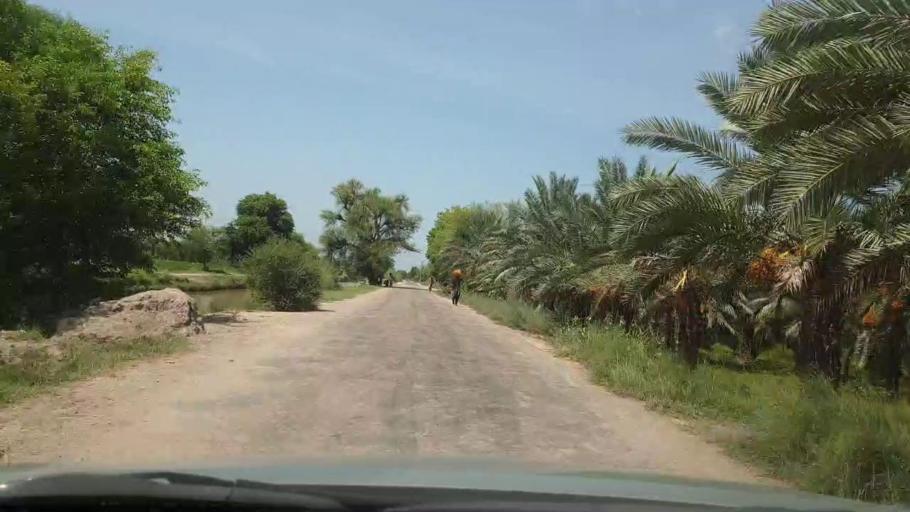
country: PK
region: Sindh
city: Pano Aqil
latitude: 27.6800
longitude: 69.1097
